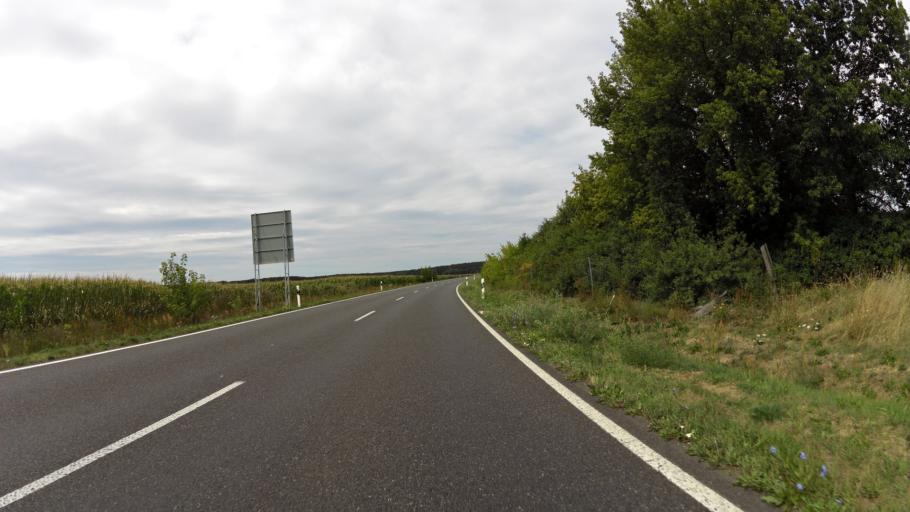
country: DE
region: Brandenburg
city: Schenkendobern
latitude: 51.8920
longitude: 14.6561
